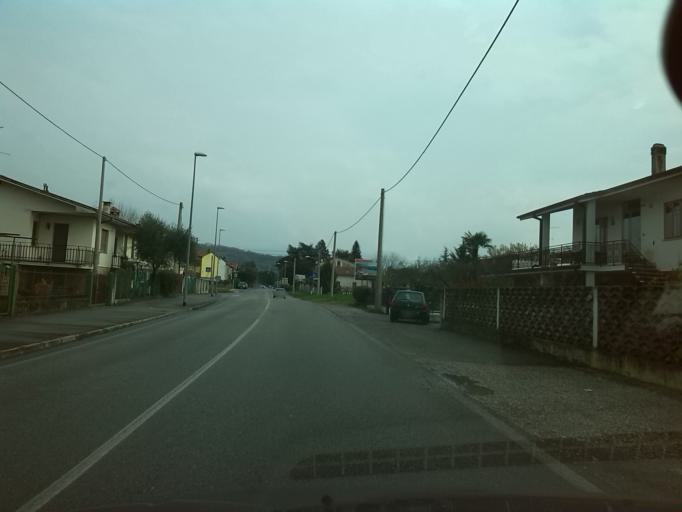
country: IT
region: Friuli Venezia Giulia
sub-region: Provincia di Gorizia
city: Mossa
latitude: 45.9353
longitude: 13.5534
